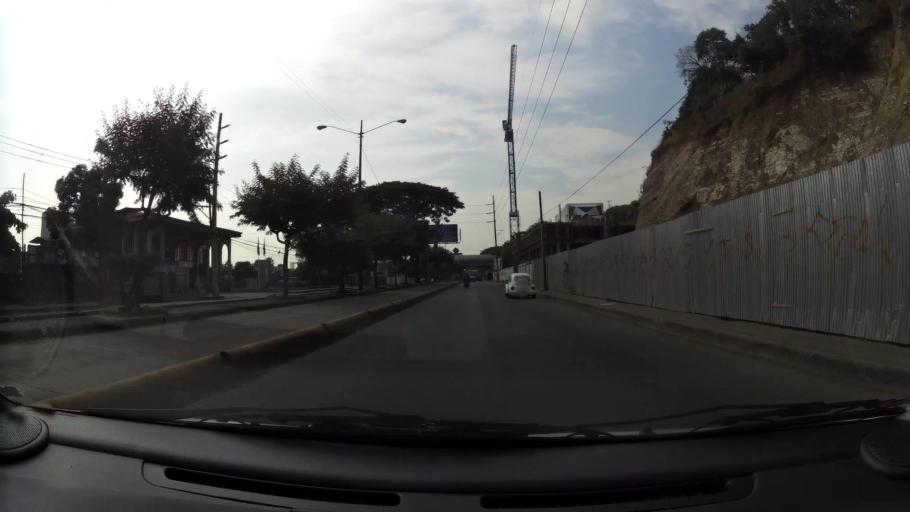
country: EC
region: Guayas
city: Guayaquil
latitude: -2.1798
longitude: -79.9054
